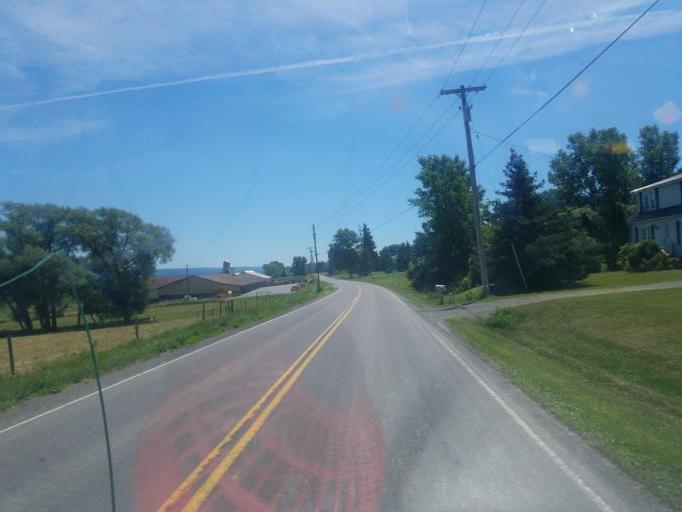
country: US
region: New York
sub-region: Yates County
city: Penn Yan
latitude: 42.6137
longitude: -76.9785
